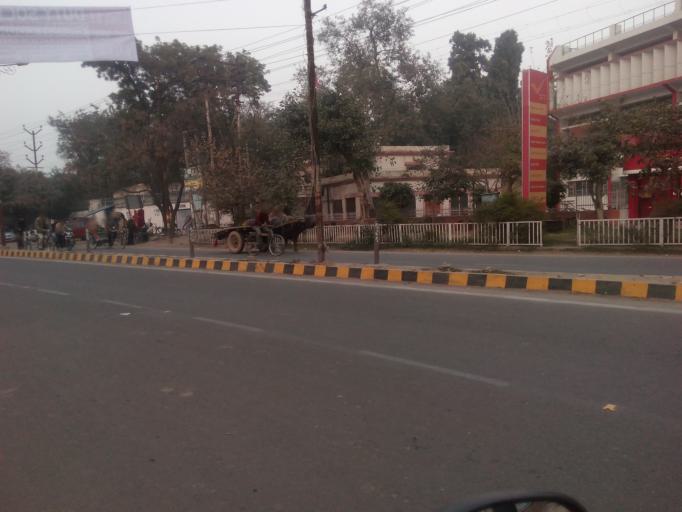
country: IN
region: Uttar Pradesh
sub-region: Aligarh
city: Aligarh
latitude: 27.8886
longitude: 78.0704
